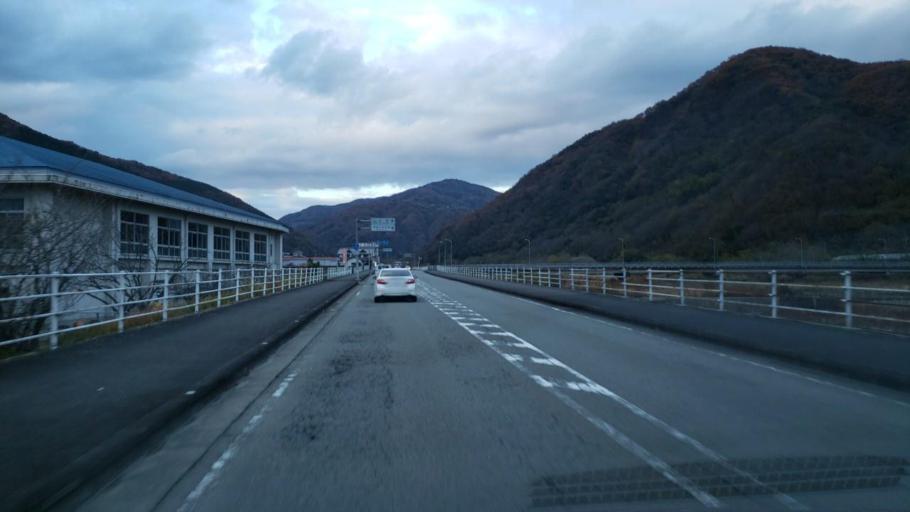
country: JP
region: Tokushima
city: Wakimachi
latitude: 34.0891
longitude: 134.1730
